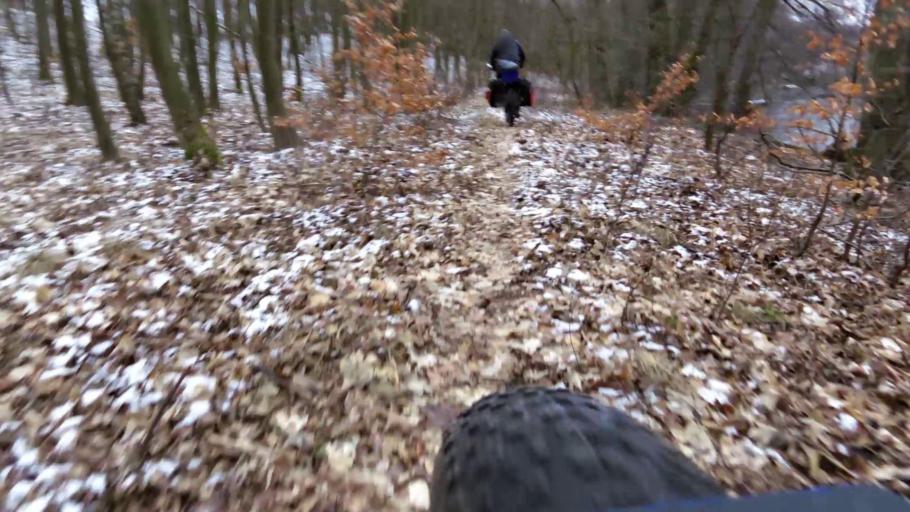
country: PL
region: West Pomeranian Voivodeship
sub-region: Powiat walecki
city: Miroslawiec
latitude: 53.3507
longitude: 16.2650
